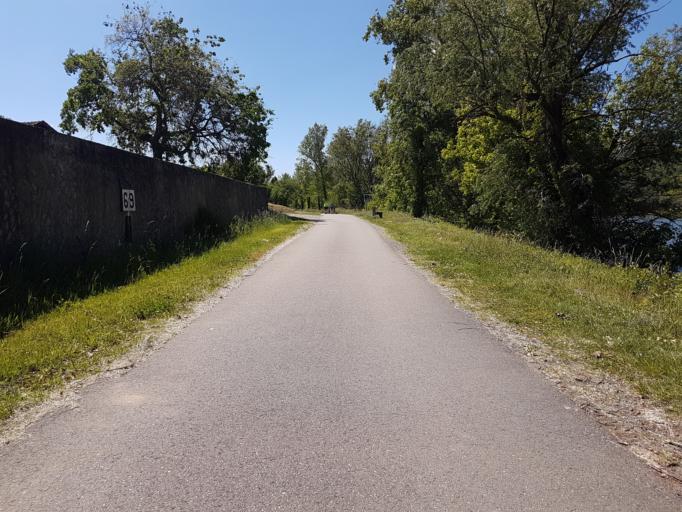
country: FR
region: Rhone-Alpes
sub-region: Departement de la Drome
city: Andancette
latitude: 45.2401
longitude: 4.8031
